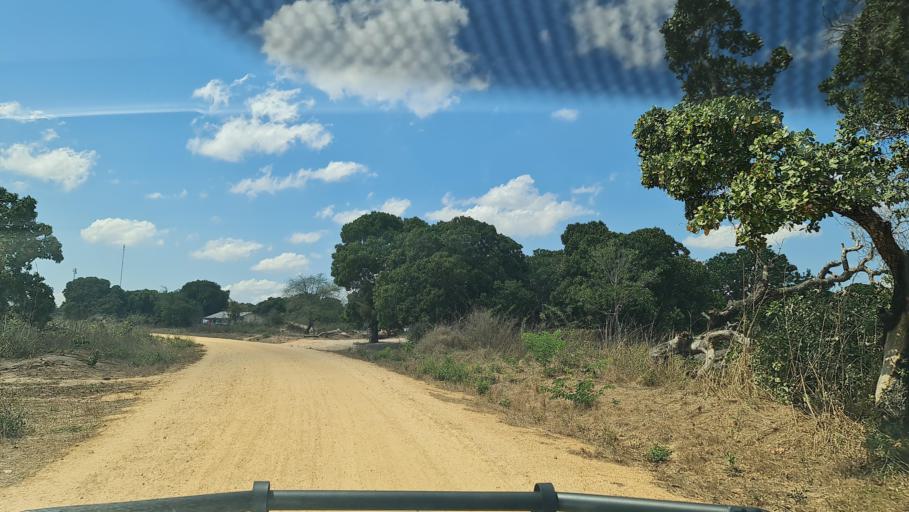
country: MZ
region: Nampula
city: Nacala
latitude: -14.1710
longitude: 40.2573
